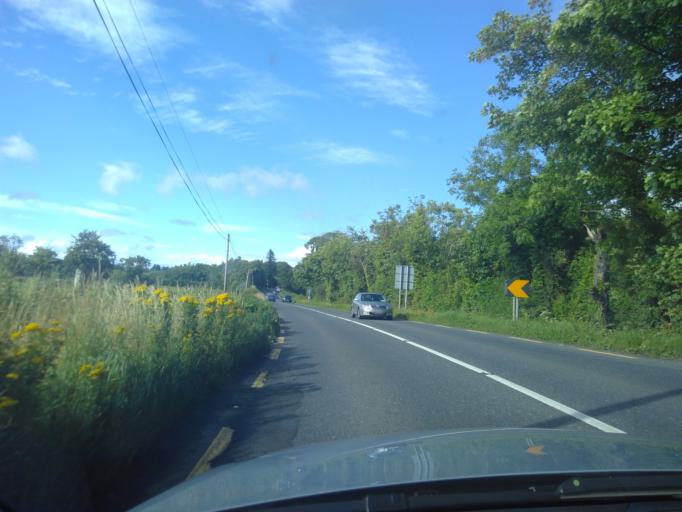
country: IE
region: Ulster
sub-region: County Donegal
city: Ballybofey
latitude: 54.8244
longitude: -7.7511
